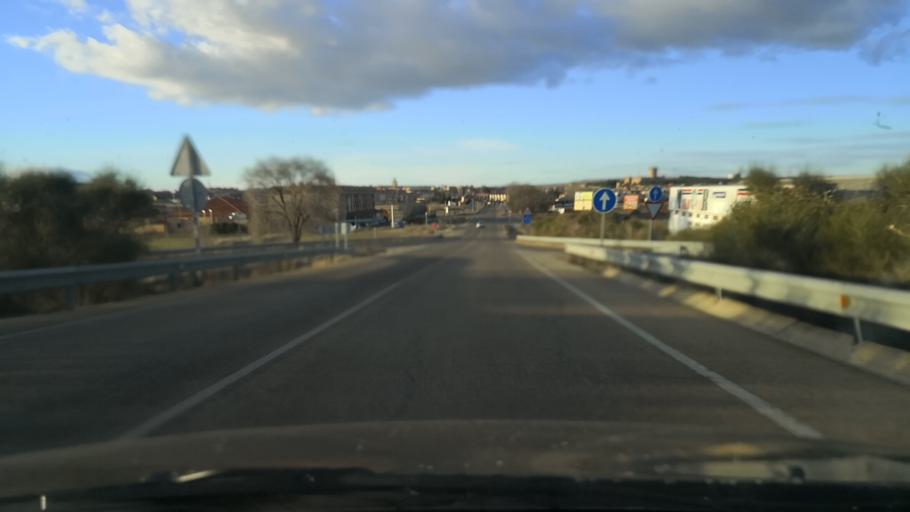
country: ES
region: Castille and Leon
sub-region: Provincia de Valladolid
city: Medina del Campo
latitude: 41.2944
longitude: -4.9025
